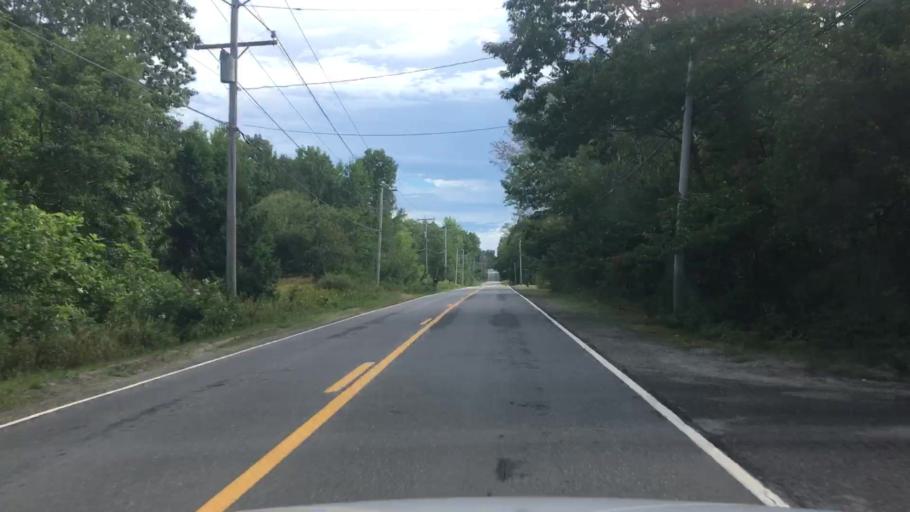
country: US
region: Maine
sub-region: Hancock County
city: Ellsworth
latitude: 44.4950
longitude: -68.4203
